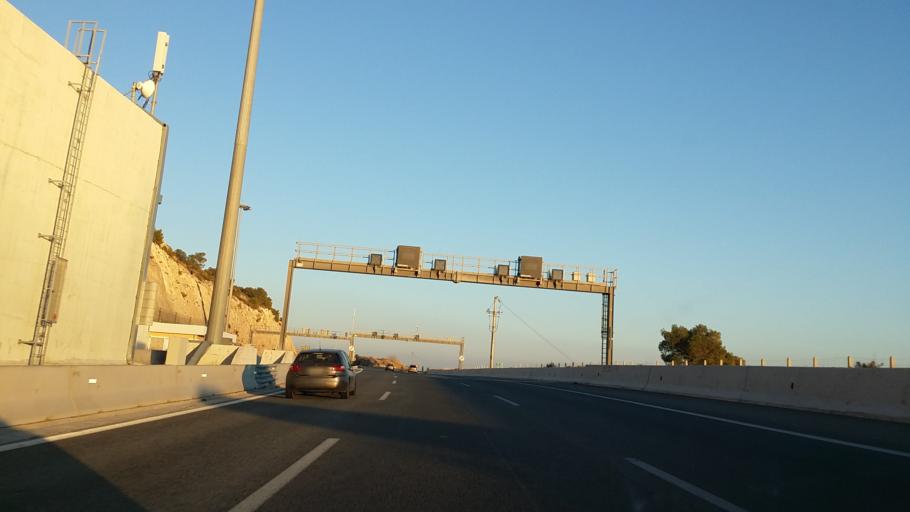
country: GR
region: Attica
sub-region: Nomarchia Dytikis Attikis
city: Megara
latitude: 37.9729
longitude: 23.3020
